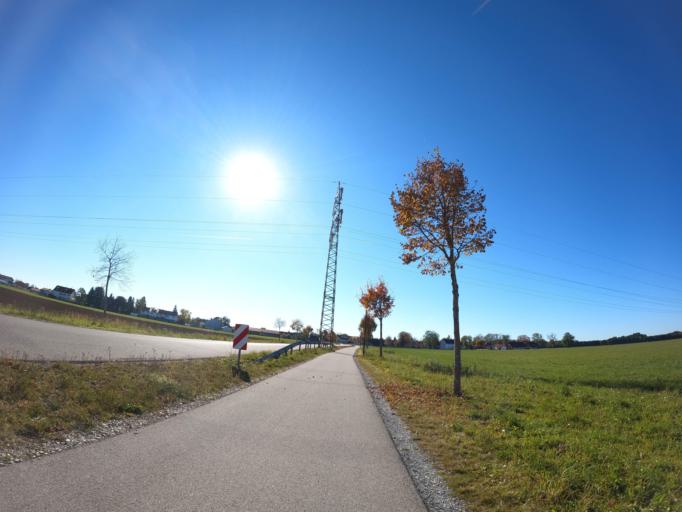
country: DE
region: Bavaria
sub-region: Upper Bavaria
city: Putzbrunn
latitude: 48.0879
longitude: 11.7008
